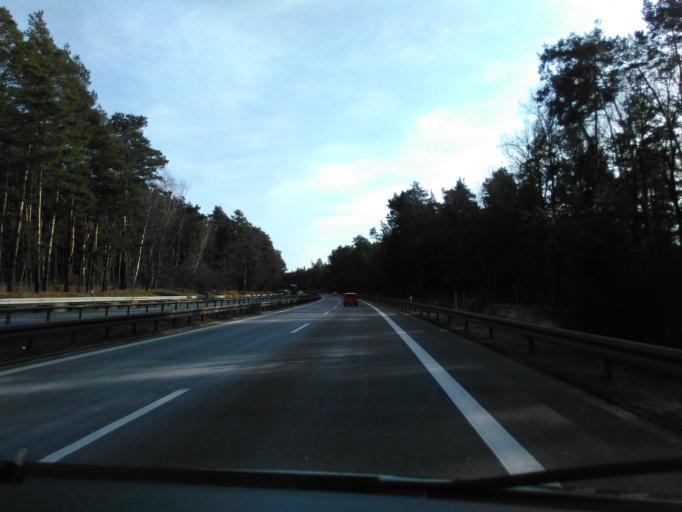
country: DE
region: Brandenburg
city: Calau
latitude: 51.7417
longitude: 13.8621
